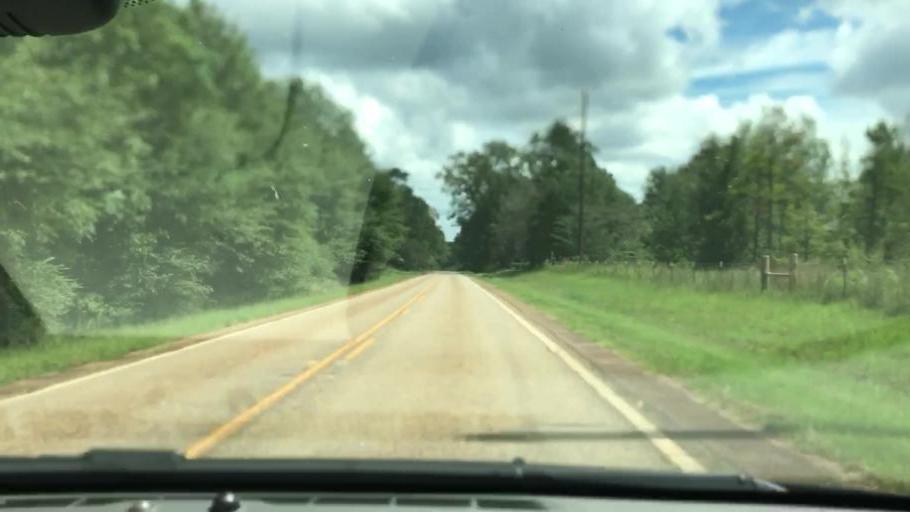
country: US
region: Georgia
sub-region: Stewart County
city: Lumpkin
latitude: 32.0697
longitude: -84.8844
